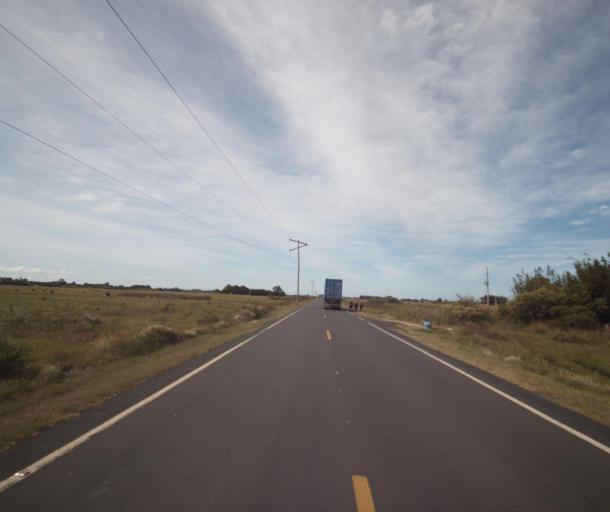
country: BR
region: Rio Grande do Sul
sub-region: Rio Grande
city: Rio Grande
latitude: -31.9409
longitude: -51.9724
